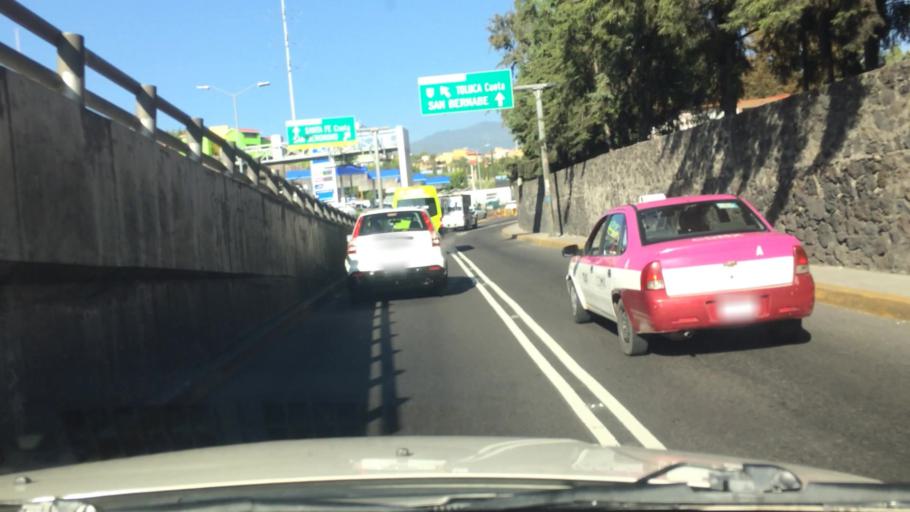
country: MX
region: Mexico City
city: Magdalena Contreras
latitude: 19.3167
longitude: -99.2322
